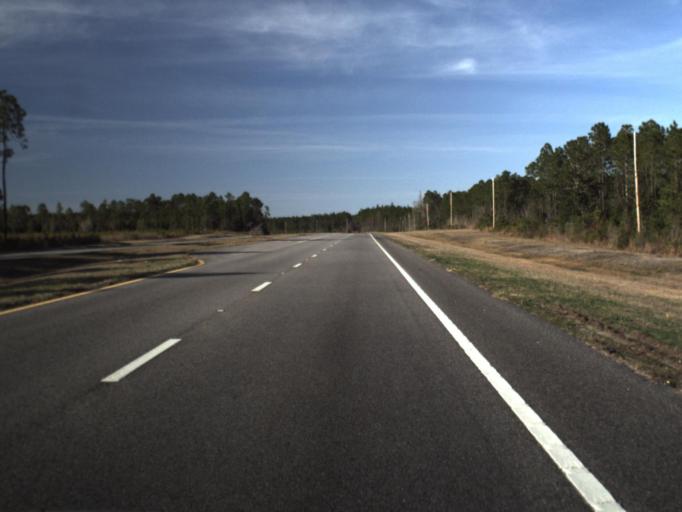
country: US
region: Florida
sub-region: Bay County
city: Laguna Beach
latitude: 30.3592
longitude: -85.8588
